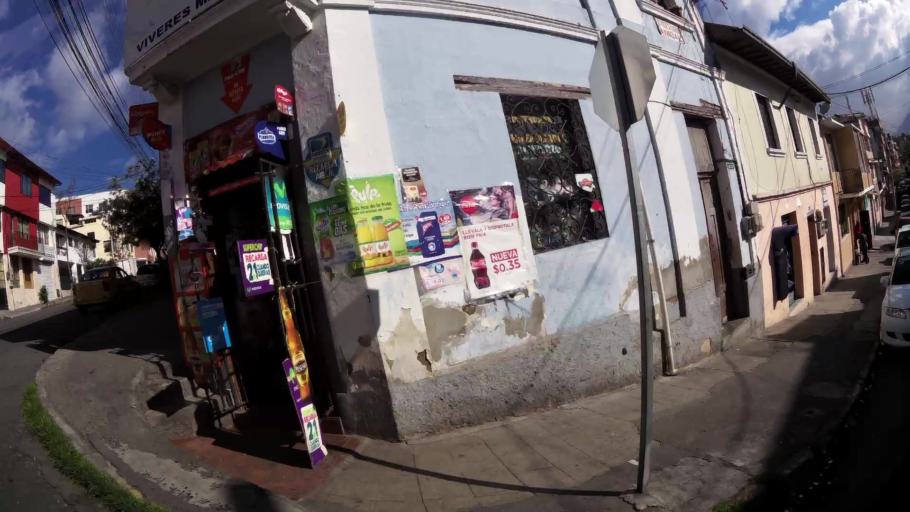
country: EC
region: Pichincha
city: Quito
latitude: -0.2161
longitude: -78.4951
